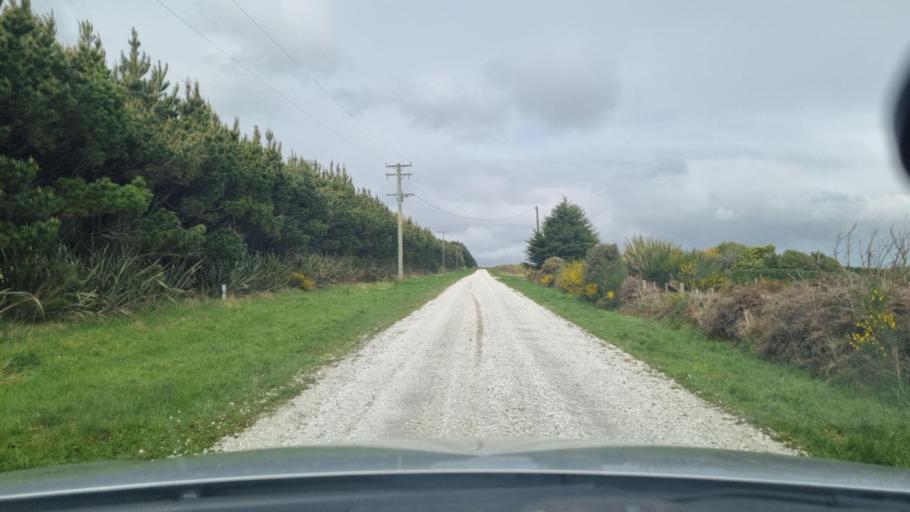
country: NZ
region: Southland
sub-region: Invercargill City
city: Bluff
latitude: -46.5125
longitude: 168.3538
